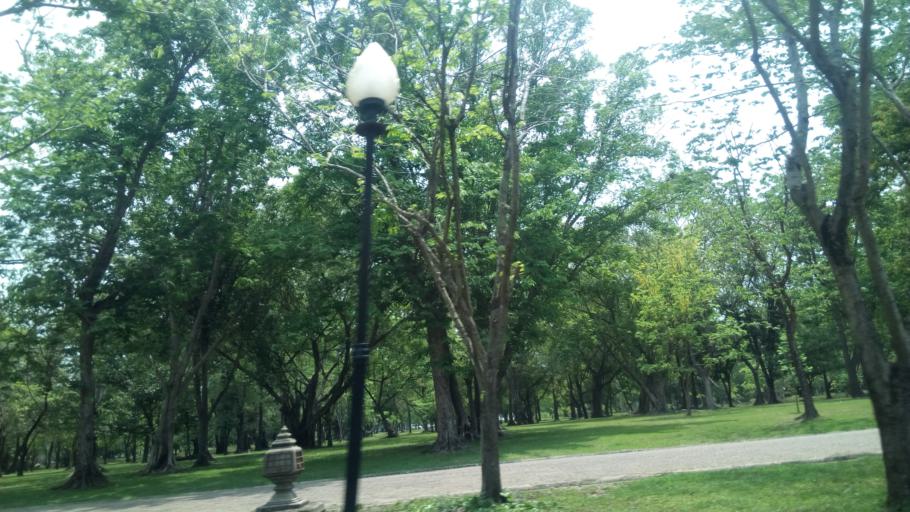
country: TH
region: Bangkok
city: Thawi Watthana
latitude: 13.7773
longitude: 100.3171
